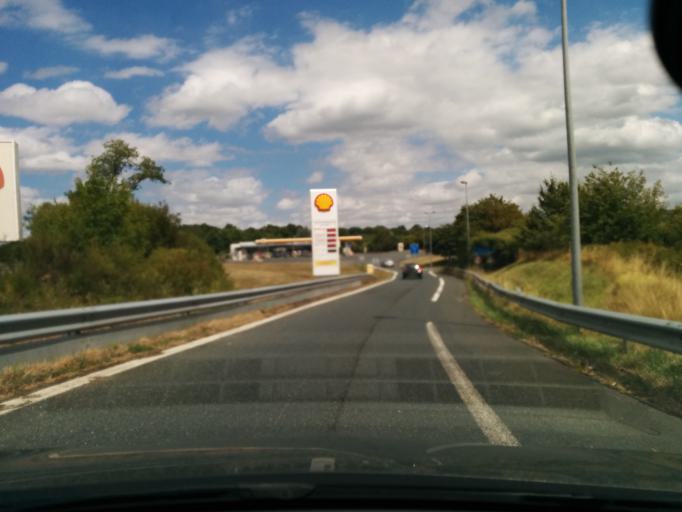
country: FR
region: Centre
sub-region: Departement de l'Indre
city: Luant
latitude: 46.7218
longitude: 1.6016
